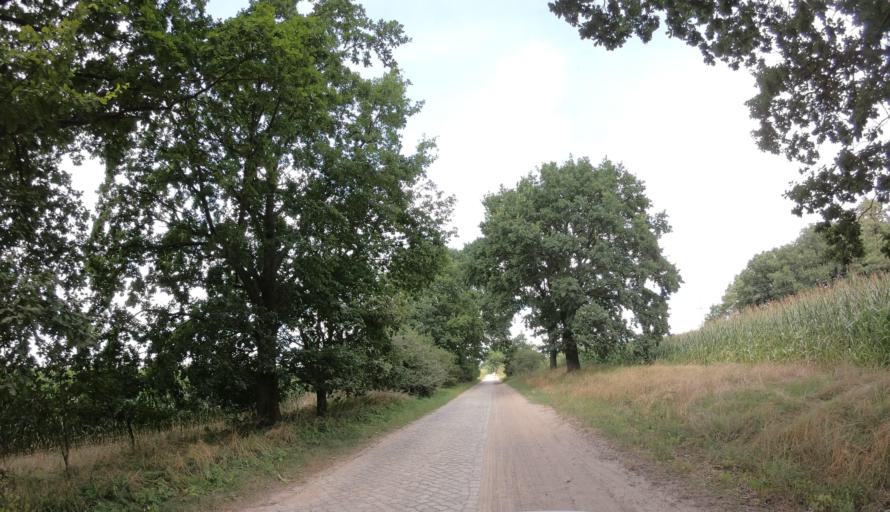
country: PL
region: West Pomeranian Voivodeship
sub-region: Powiat stargardzki
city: Kobylanka
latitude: 53.3140
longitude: 14.8298
